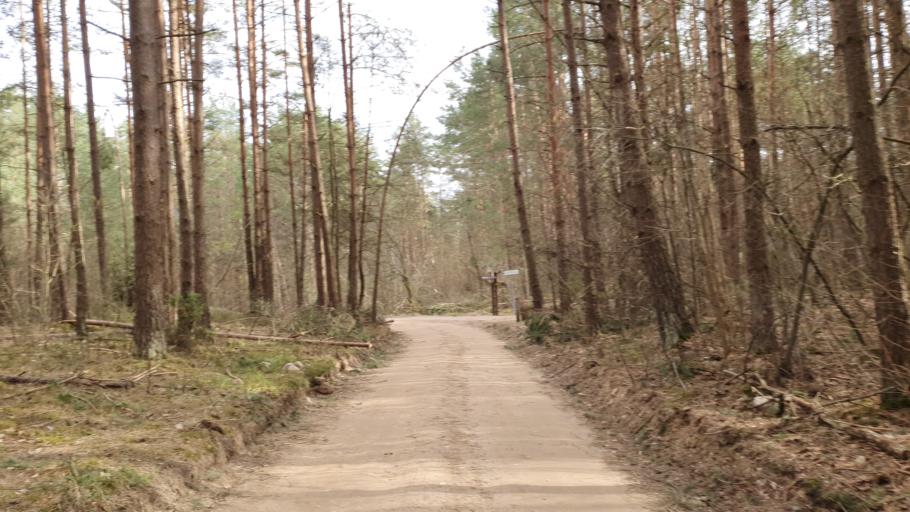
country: LT
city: Grigiskes
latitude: 54.7309
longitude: 25.0287
